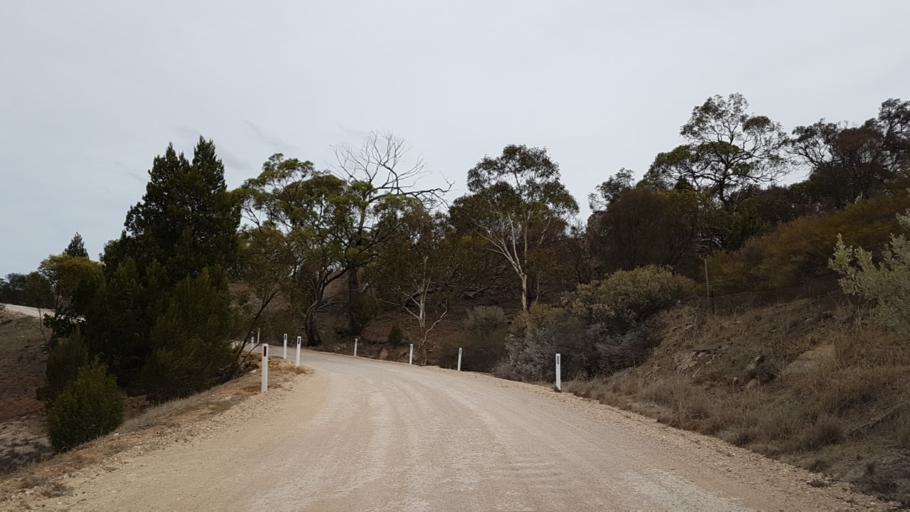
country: AU
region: South Australia
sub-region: Mount Barker
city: Callington
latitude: -35.0027
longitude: 139.0847
